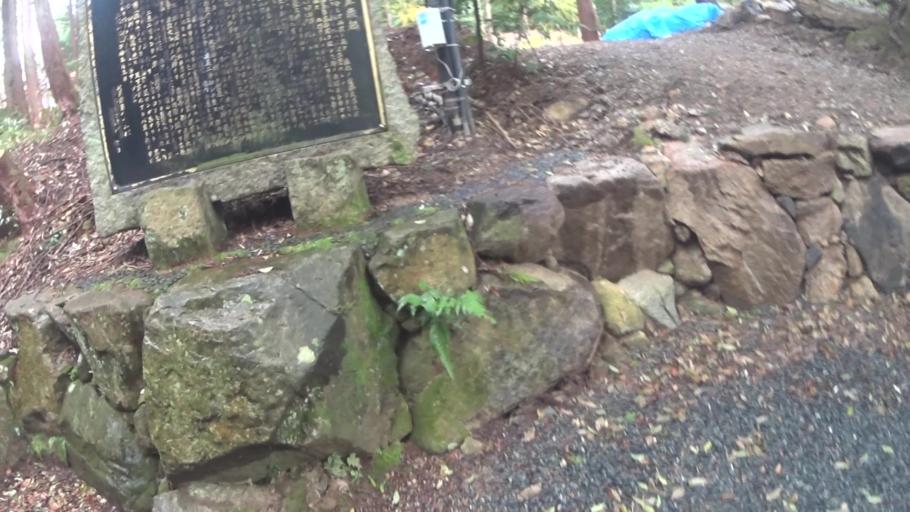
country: JP
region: Kyoto
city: Miyazu
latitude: 35.5861
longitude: 135.1985
